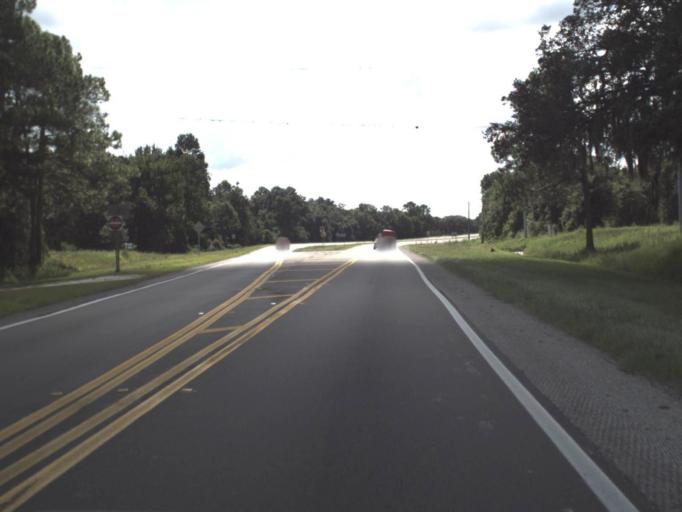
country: US
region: Florida
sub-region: Polk County
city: Gibsonia
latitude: 28.1684
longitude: -81.9782
